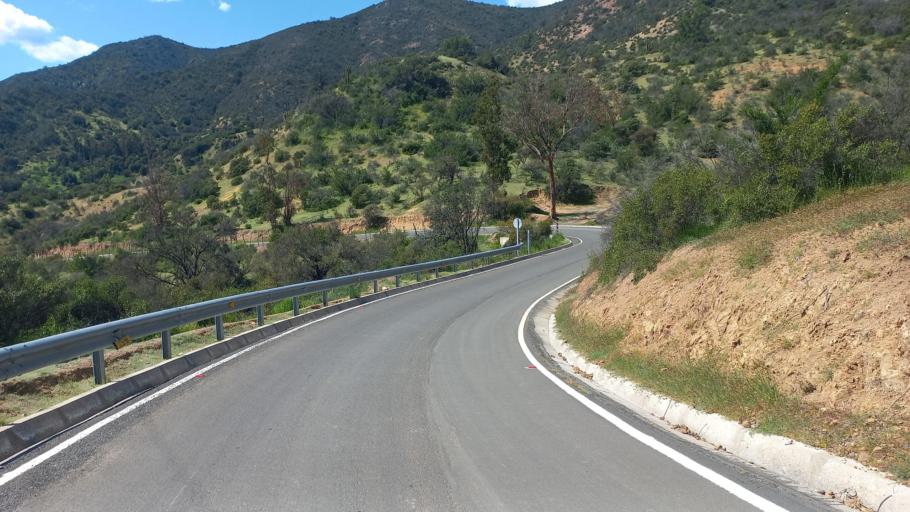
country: CL
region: Santiago Metropolitan
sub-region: Provincia de Chacabuco
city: Lampa
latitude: -33.1930
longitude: -71.0912
